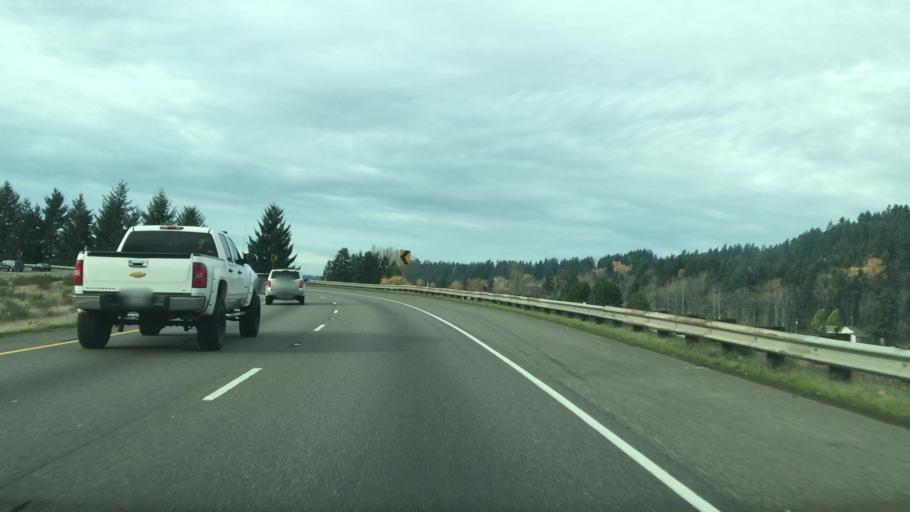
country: US
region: Washington
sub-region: Pierce County
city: North Puyallup
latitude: 47.2031
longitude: -122.2743
